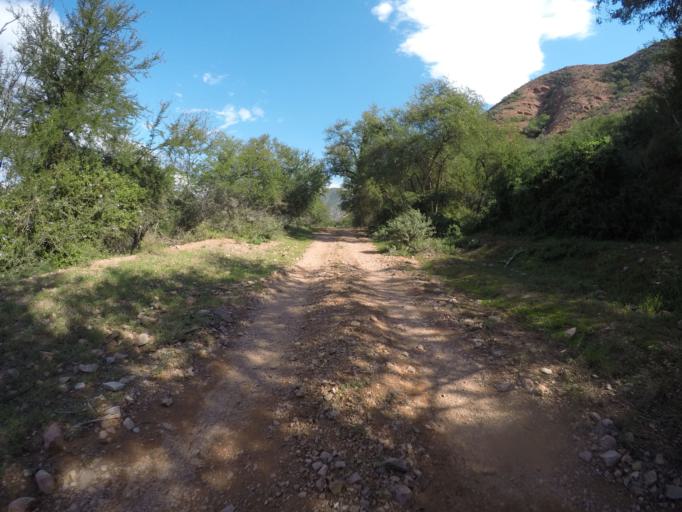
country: ZA
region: Eastern Cape
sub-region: Cacadu District Municipality
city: Kareedouw
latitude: -33.6621
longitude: 24.3935
